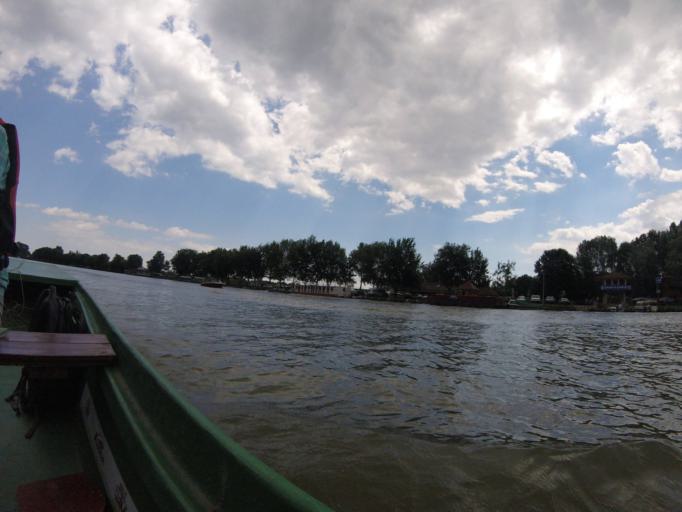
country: HU
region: Jasz-Nagykun-Szolnok
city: Tiszaszolos
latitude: 47.6052
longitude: 20.7114
